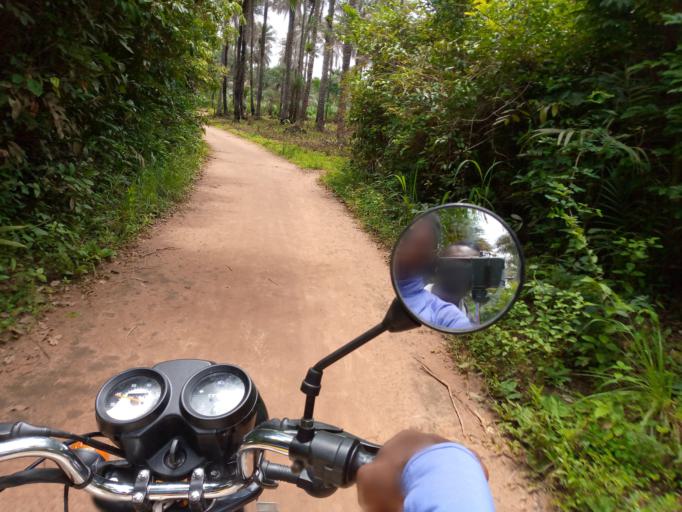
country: SL
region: Northern Province
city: Mange
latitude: 8.9757
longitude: -12.8213
